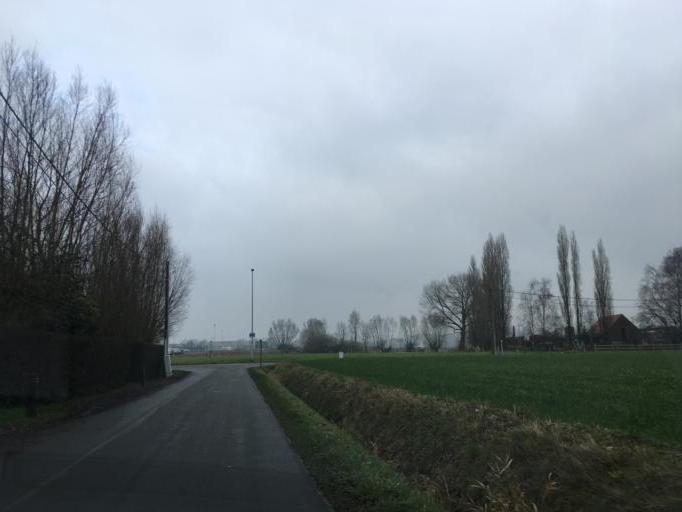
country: BE
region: Flanders
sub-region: Provincie West-Vlaanderen
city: Roeselare
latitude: 50.9762
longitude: 3.1366
